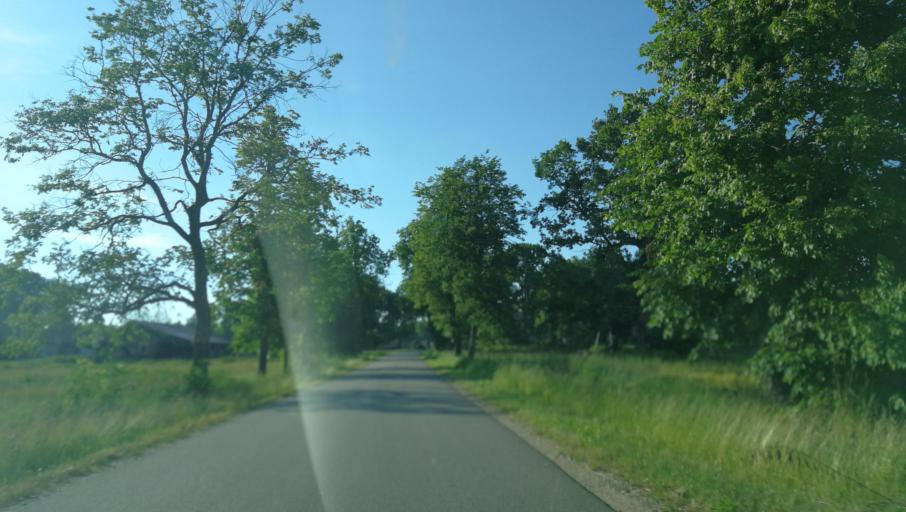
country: LV
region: Pargaujas
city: Stalbe
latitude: 57.3571
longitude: 25.0899
